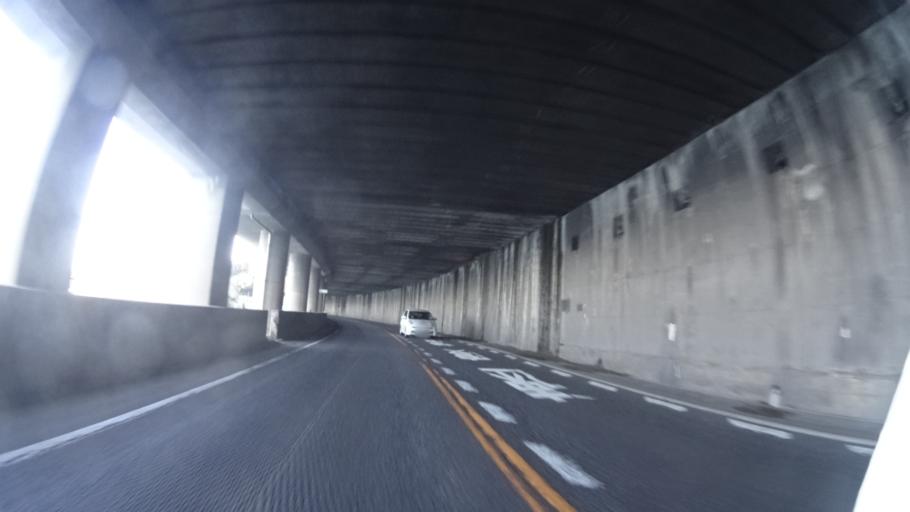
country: JP
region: Fukui
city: Tsuruga
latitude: 35.7308
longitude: 136.0970
